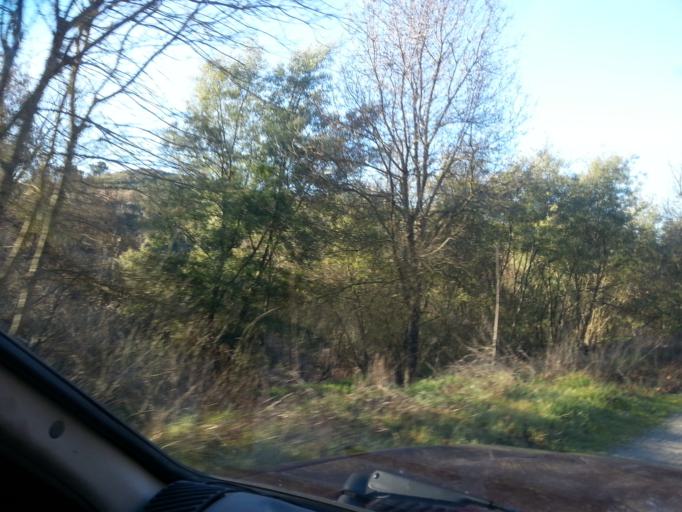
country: PT
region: Guarda
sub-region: Fornos de Algodres
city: Fornos de Algodres
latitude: 40.6071
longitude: -7.5338
